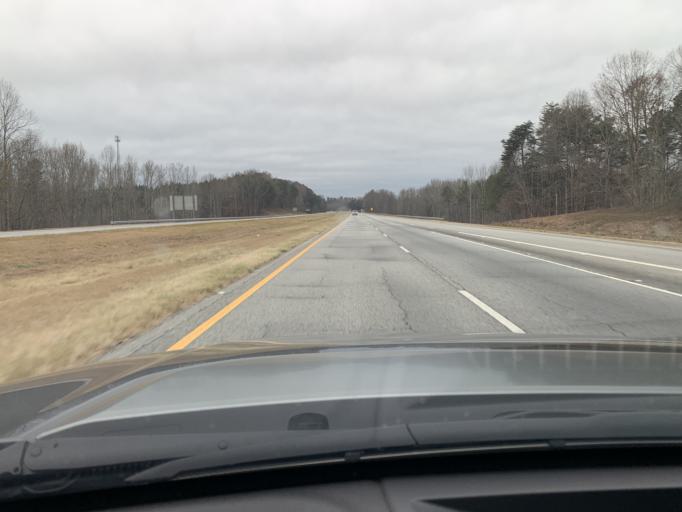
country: US
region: Georgia
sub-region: Habersham County
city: Baldwin
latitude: 34.5127
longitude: -83.5582
